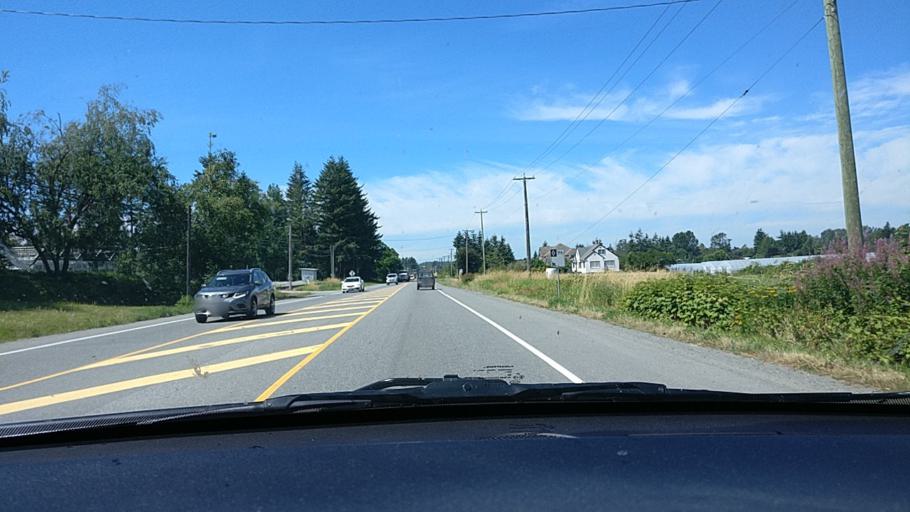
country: CA
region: British Columbia
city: Aldergrove
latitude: 49.0572
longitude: -122.4409
